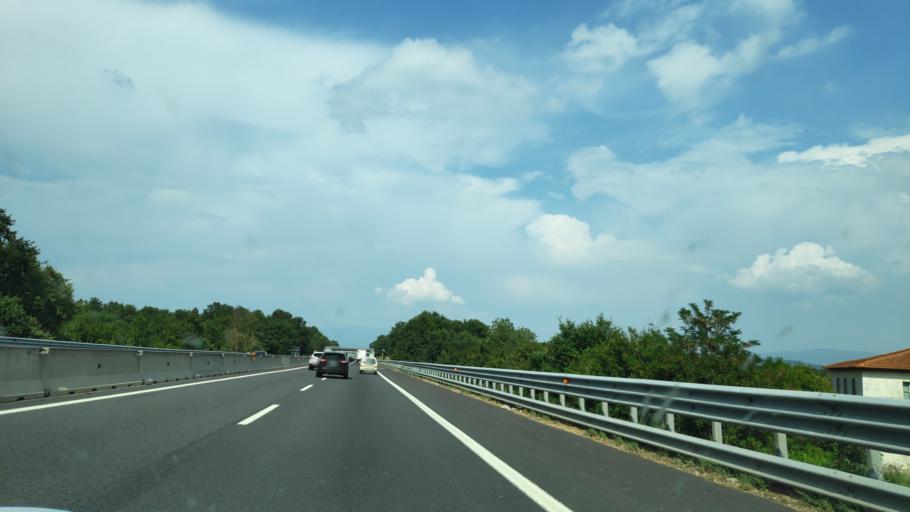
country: IT
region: Tuscany
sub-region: Province of Arezzo
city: Badia al Pino
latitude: 43.4145
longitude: 11.7684
